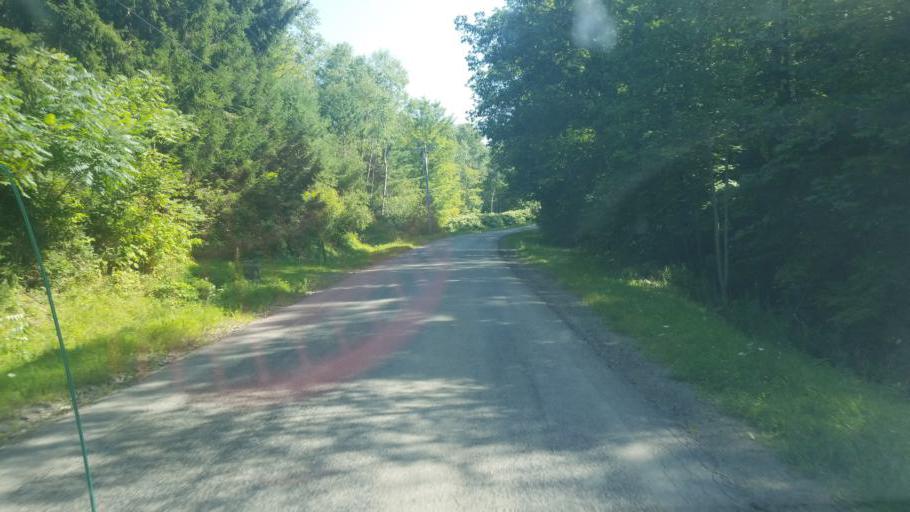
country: US
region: New York
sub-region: Allegany County
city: Bolivar
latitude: 42.0747
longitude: -78.0605
